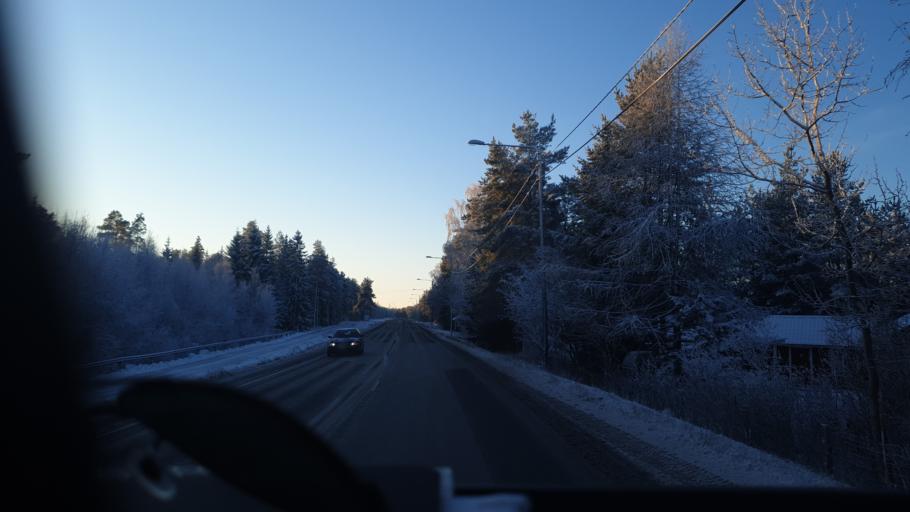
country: FI
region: Northern Ostrobothnia
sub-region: Ylivieska
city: Himanka
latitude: 64.2064
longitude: 23.7639
